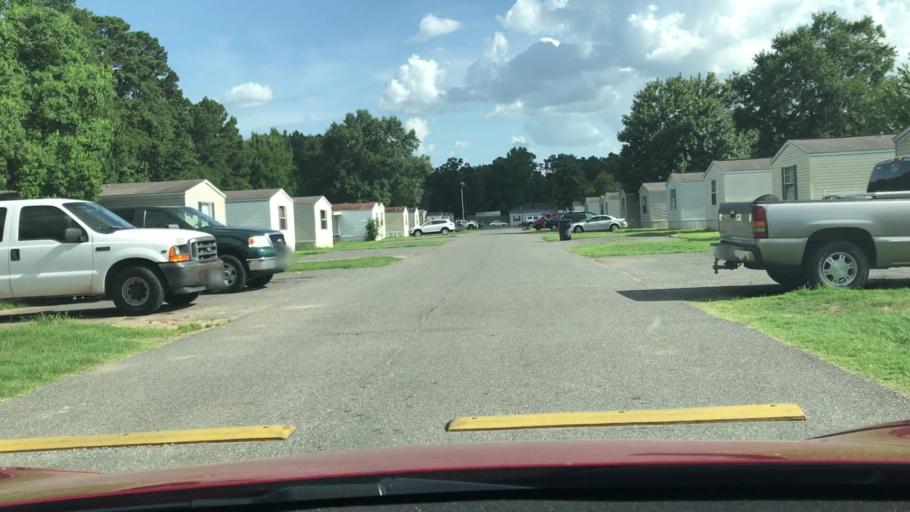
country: US
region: Louisiana
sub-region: De Soto Parish
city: Stonewall
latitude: 32.3901
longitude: -93.7661
